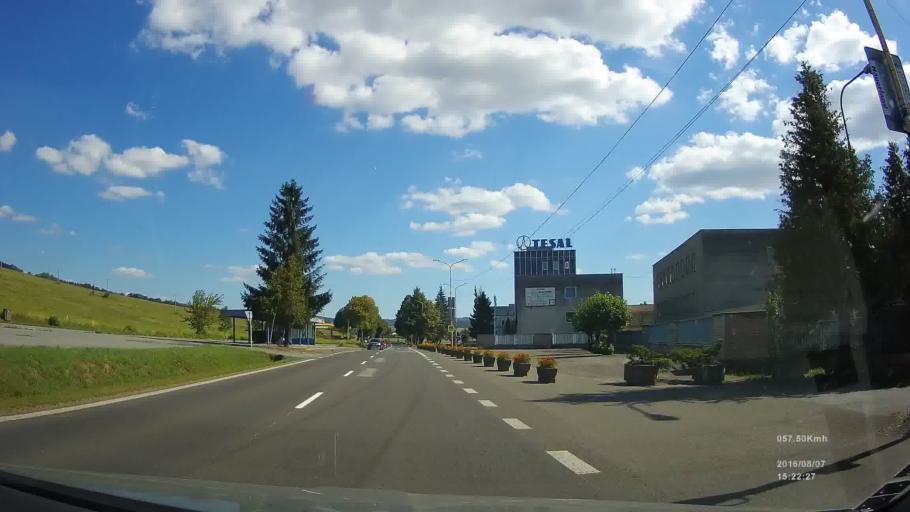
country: SK
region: Presovsky
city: Stropkov
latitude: 49.1924
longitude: 21.6560
